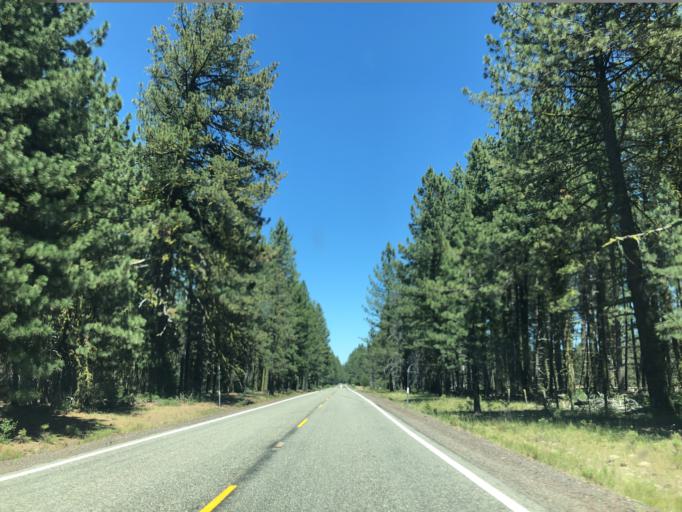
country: US
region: California
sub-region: Shasta County
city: Burney
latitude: 40.6057
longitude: -121.5245
